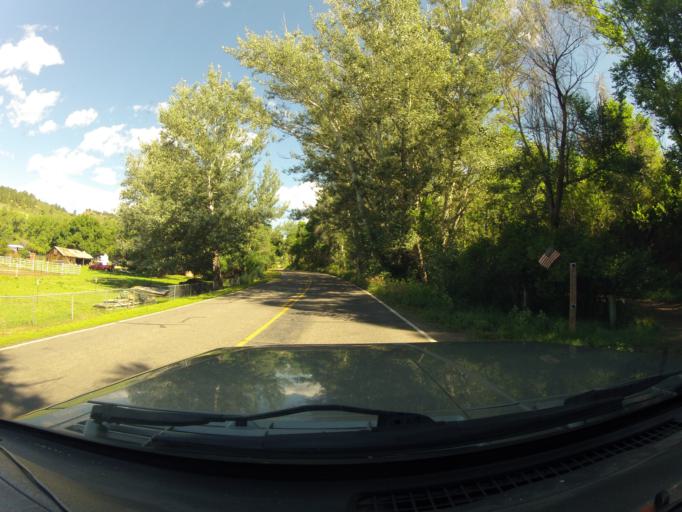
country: US
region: Colorado
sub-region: Larimer County
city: Laporte
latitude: 40.4912
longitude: -105.2178
